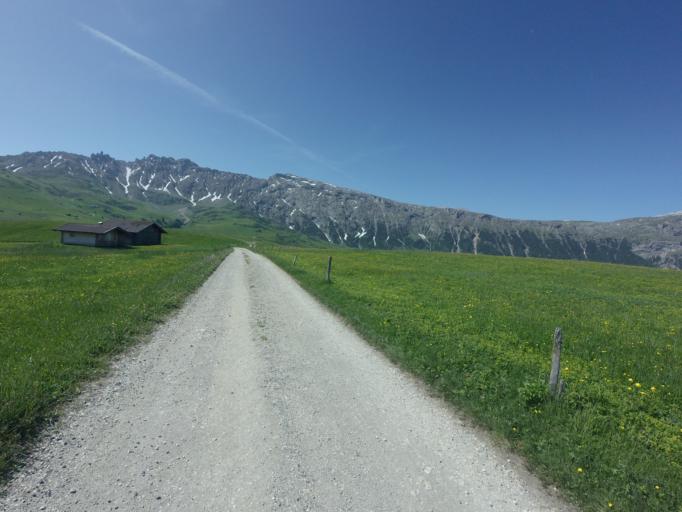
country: IT
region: Trentino-Alto Adige
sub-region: Bolzano
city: Siusi
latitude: 46.5264
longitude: 11.6217
